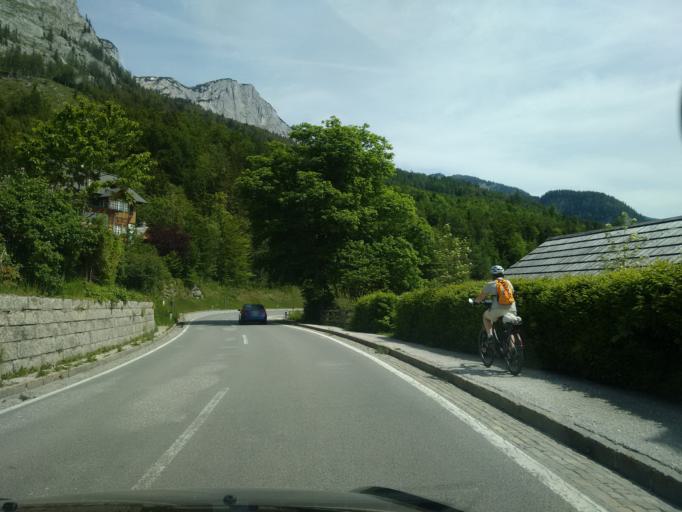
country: AT
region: Styria
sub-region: Politischer Bezirk Liezen
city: Bad Aussee
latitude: 47.6374
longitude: 13.8667
